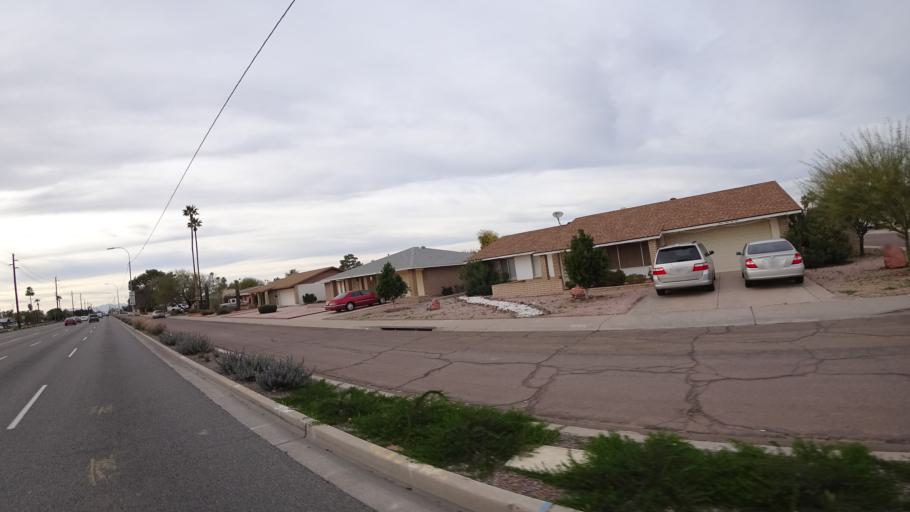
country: US
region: Arizona
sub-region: Maricopa County
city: Glendale
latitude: 33.5676
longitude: -112.1439
